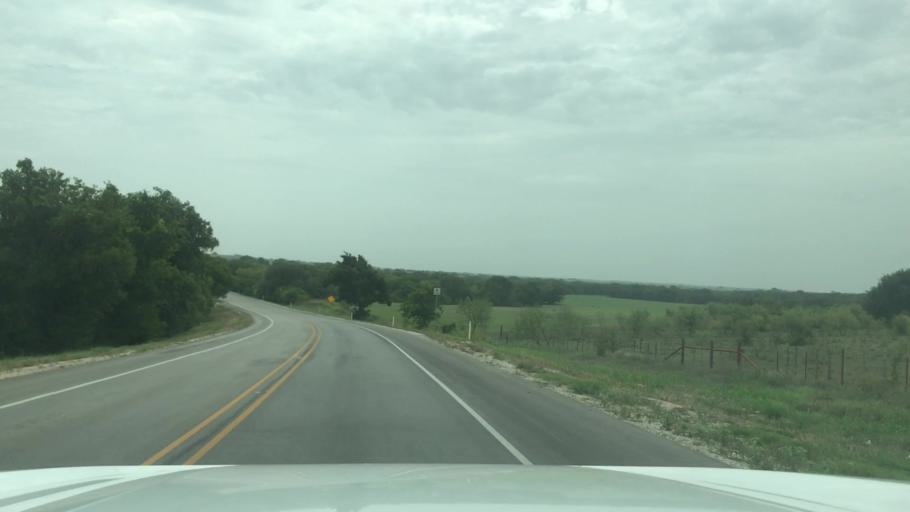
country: US
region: Texas
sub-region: Erath County
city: Dublin
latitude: 32.0753
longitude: -98.2340
